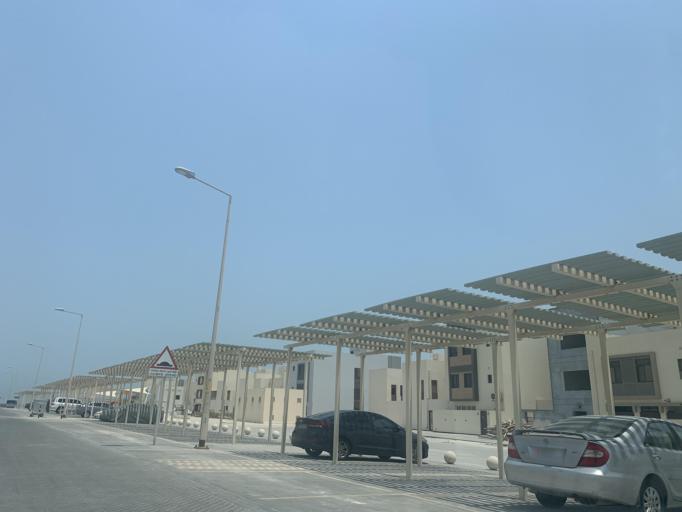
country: BH
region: Muharraq
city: Al Hadd
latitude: 26.2362
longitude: 50.6745
